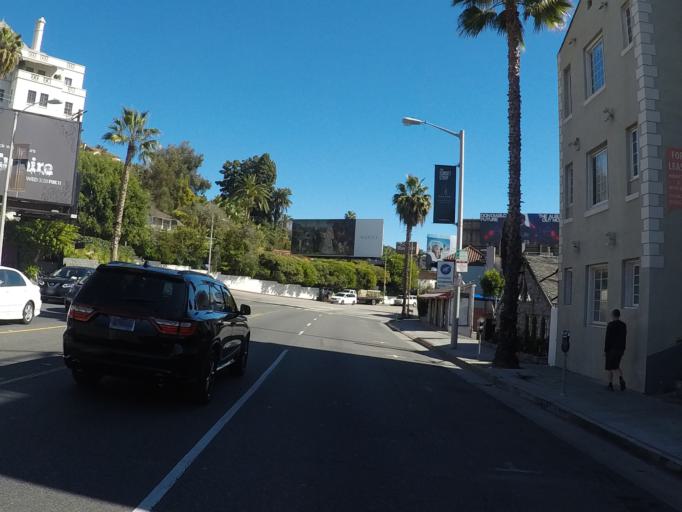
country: US
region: California
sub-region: Los Angeles County
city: West Hollywood
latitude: 34.0974
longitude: -118.3703
